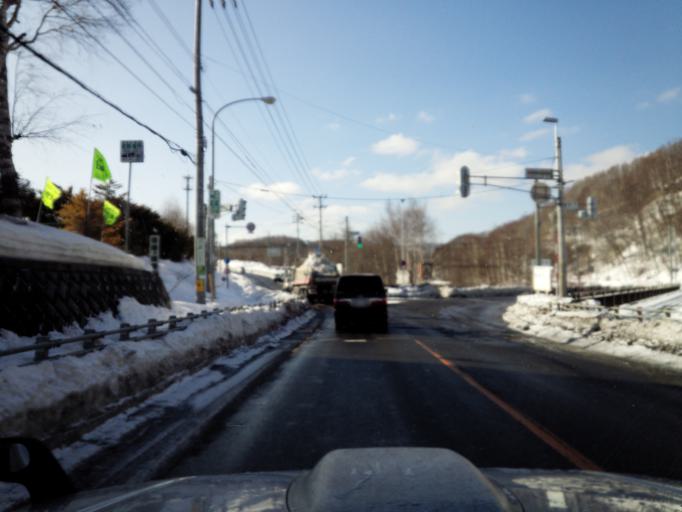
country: JP
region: Hokkaido
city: Sapporo
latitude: 42.9352
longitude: 141.3417
